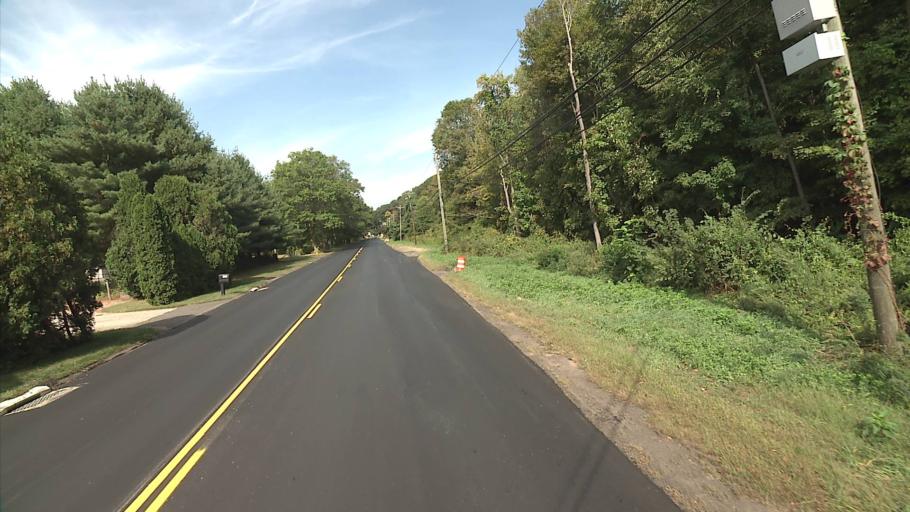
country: US
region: Connecticut
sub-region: Fairfield County
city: Shelton
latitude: 41.3503
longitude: -73.1307
